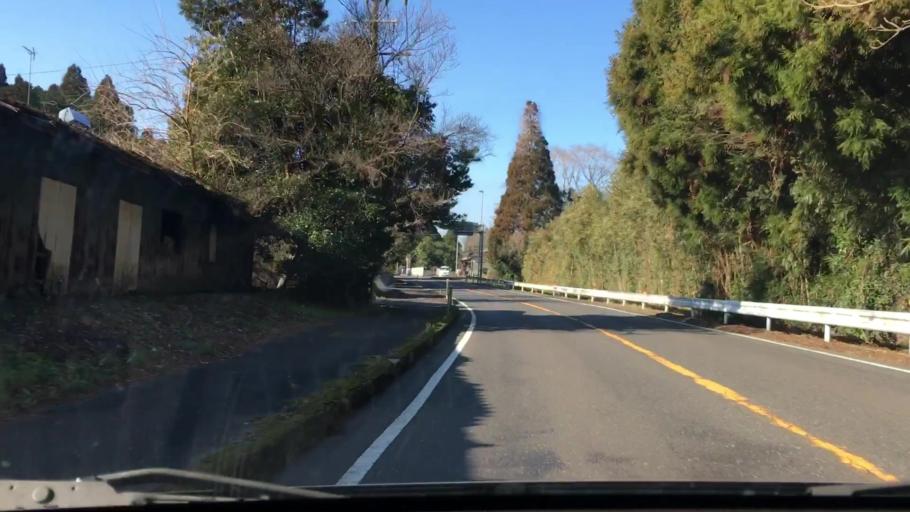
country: JP
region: Kagoshima
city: Sueyoshicho-ninokata
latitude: 31.6782
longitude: 130.9317
